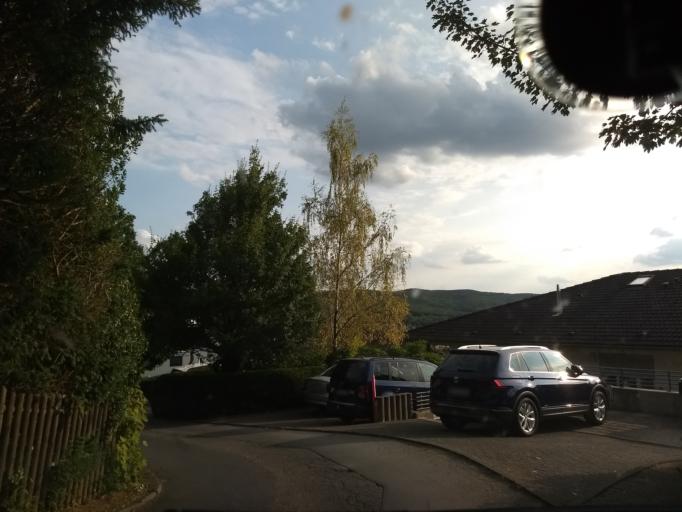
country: DE
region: North Rhine-Westphalia
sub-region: Regierungsbezirk Arnsberg
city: Arnsberg
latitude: 51.3900
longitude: 8.0812
